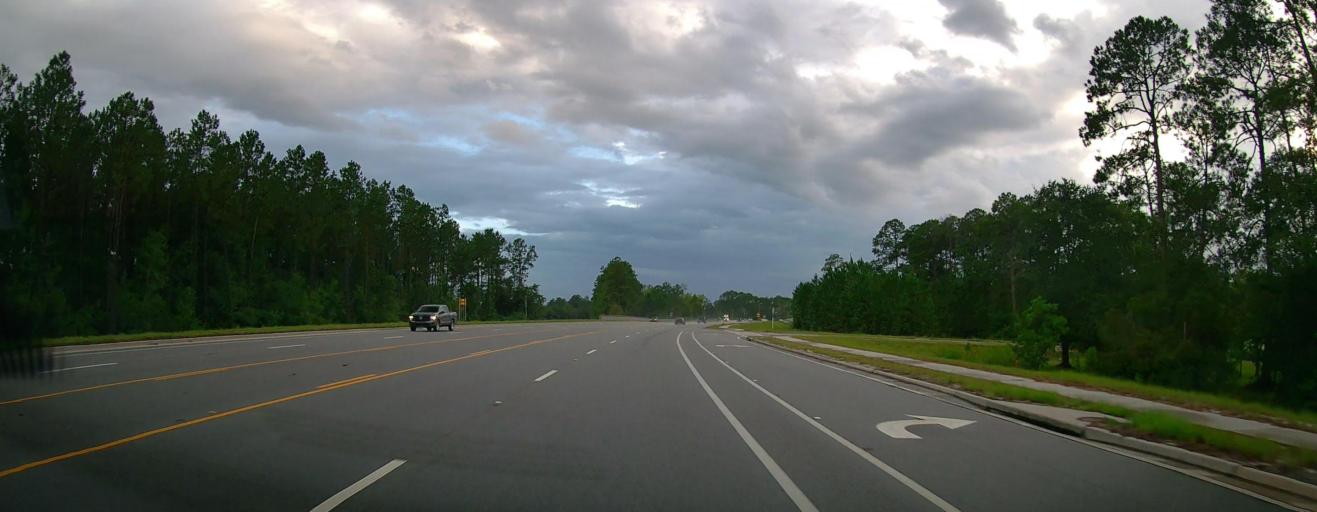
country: US
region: Georgia
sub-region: Ware County
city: Deenwood
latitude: 31.1864
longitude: -82.3914
